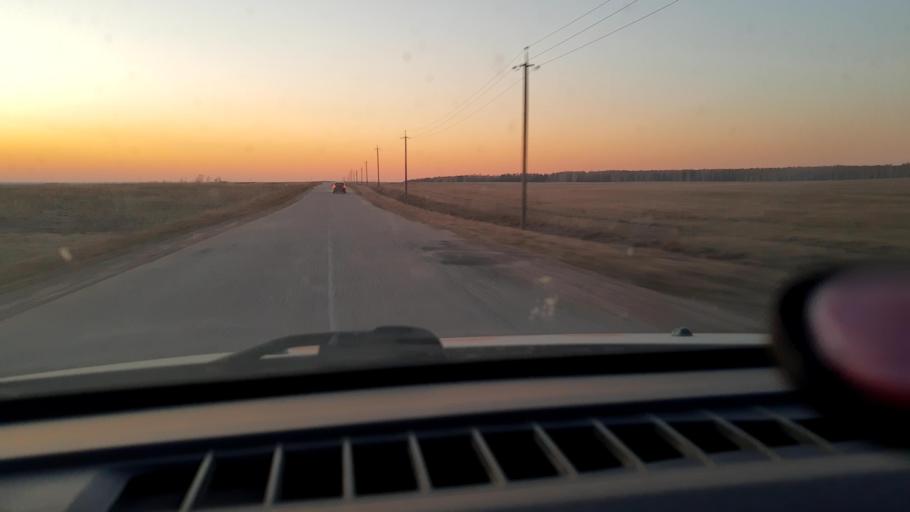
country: RU
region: Bashkortostan
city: Asanovo
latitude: 54.8087
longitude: 55.4845
